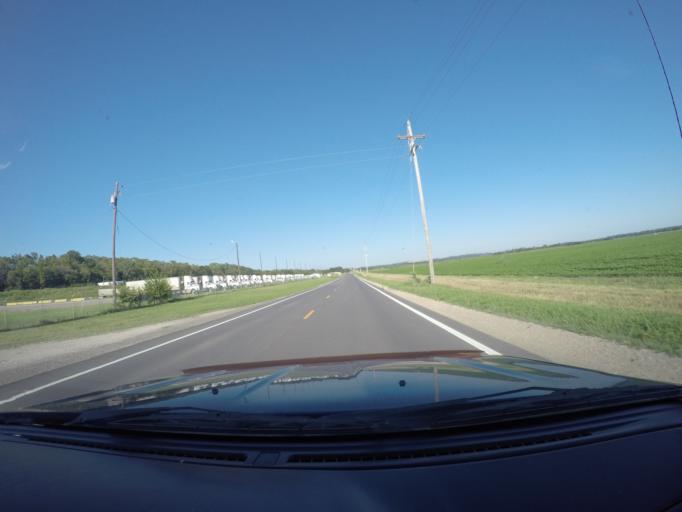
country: US
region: Kansas
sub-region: Douglas County
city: Lawrence
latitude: 39.0656
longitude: -95.3258
